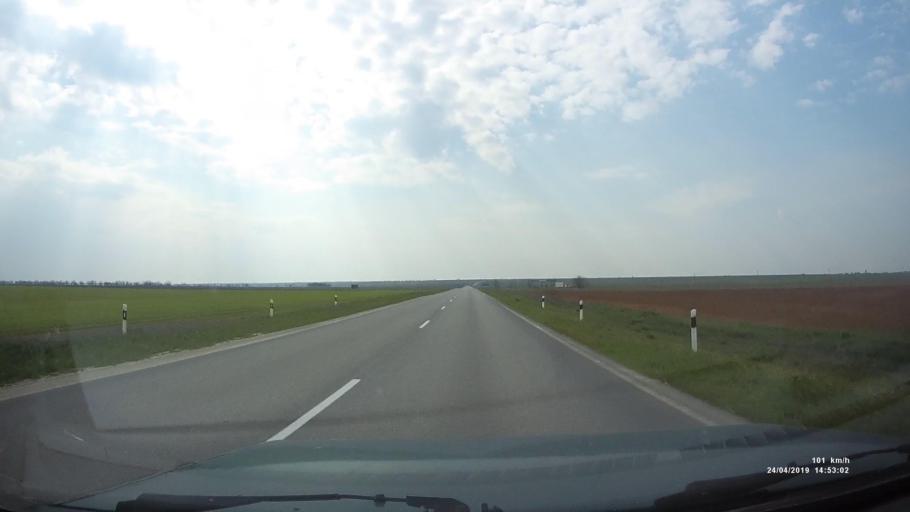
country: RU
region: Rostov
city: Remontnoye
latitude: 46.5309
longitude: 43.6678
